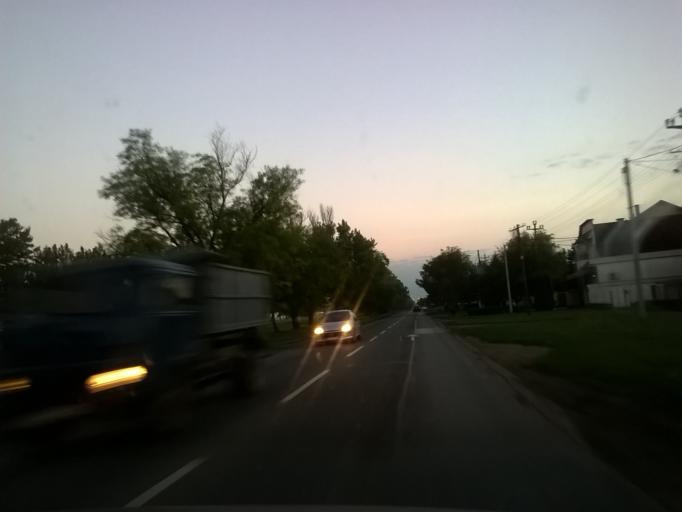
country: RS
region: Autonomna Pokrajina Vojvodina
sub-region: Juznobanatski Okrug
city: Pancevo
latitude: 44.8998
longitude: 20.6313
